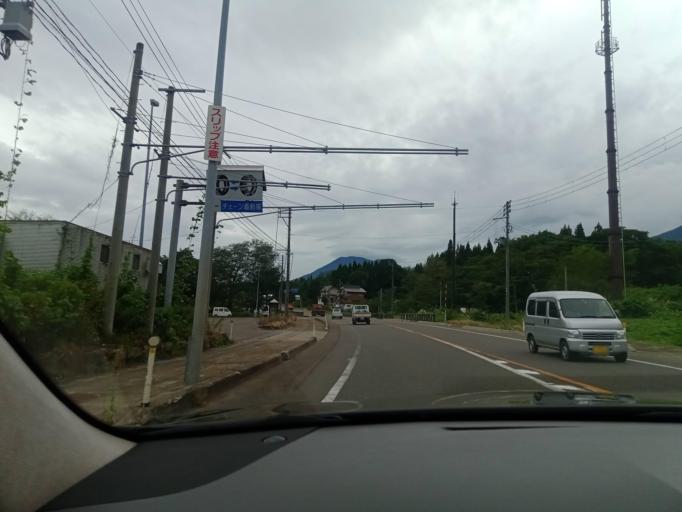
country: JP
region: Niigata
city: Arai
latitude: 36.9013
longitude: 138.2120
